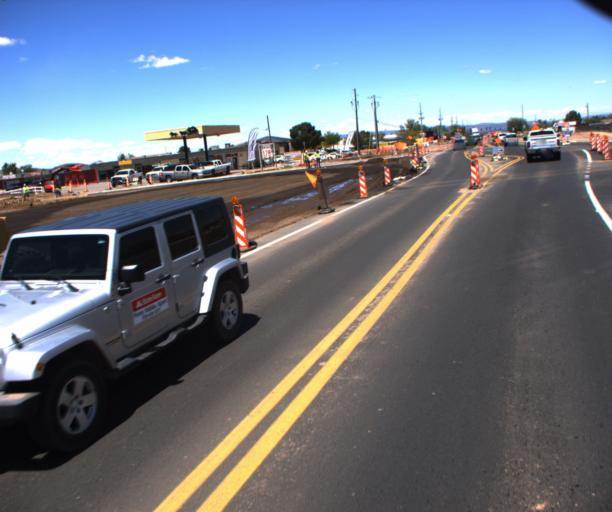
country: US
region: Arizona
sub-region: Yavapai County
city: Chino Valley
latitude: 34.7706
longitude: -112.4530
